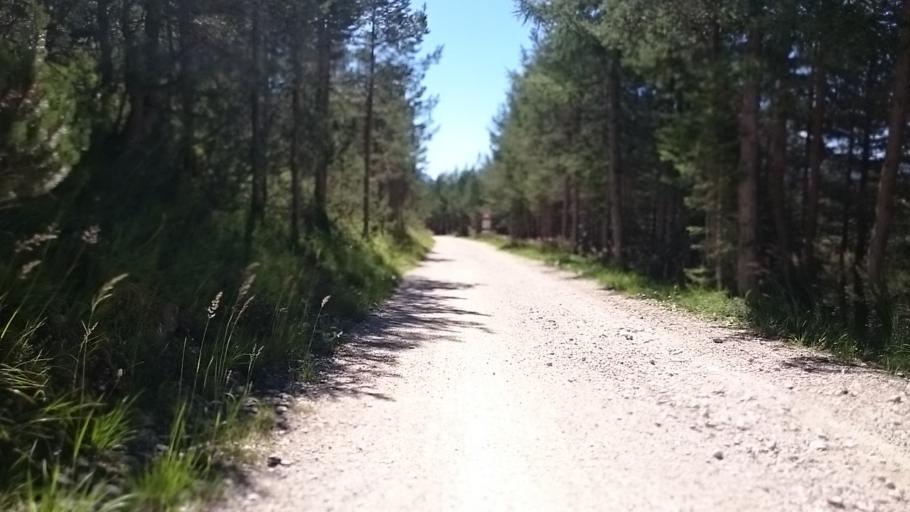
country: IT
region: Veneto
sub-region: Provincia di Belluno
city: Cortina d'Ampezzo
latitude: 46.5767
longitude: 12.1189
